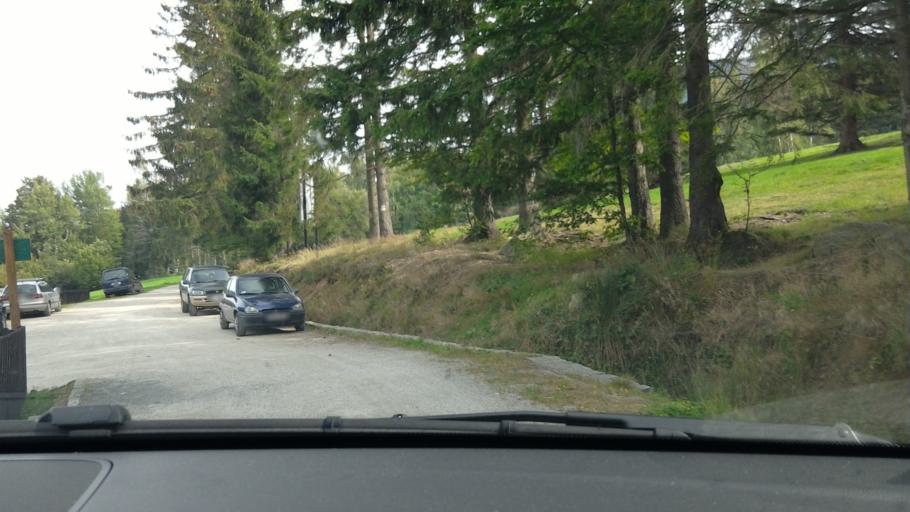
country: PL
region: Lower Silesian Voivodeship
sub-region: Powiat jeleniogorski
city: Karpacz
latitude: 50.7653
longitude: 15.7551
